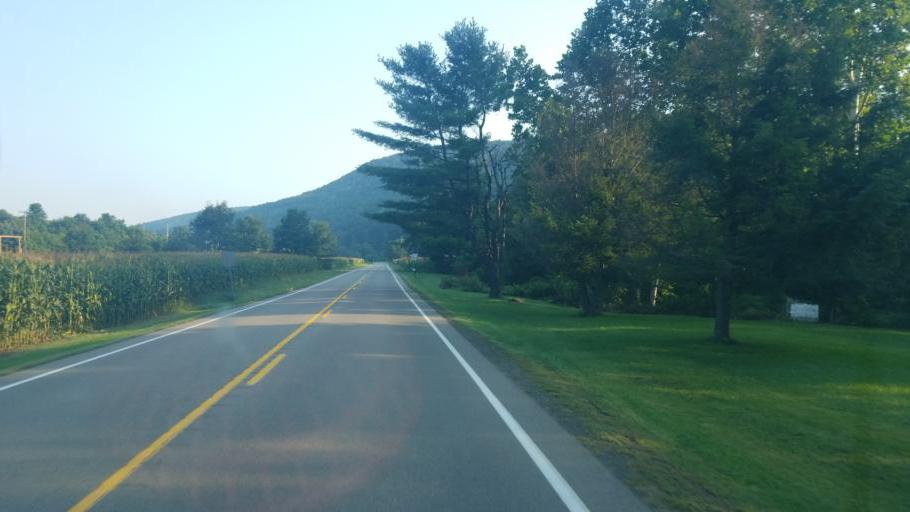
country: US
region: Pennsylvania
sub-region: Tioga County
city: Westfield
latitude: 41.9614
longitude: -77.4455
